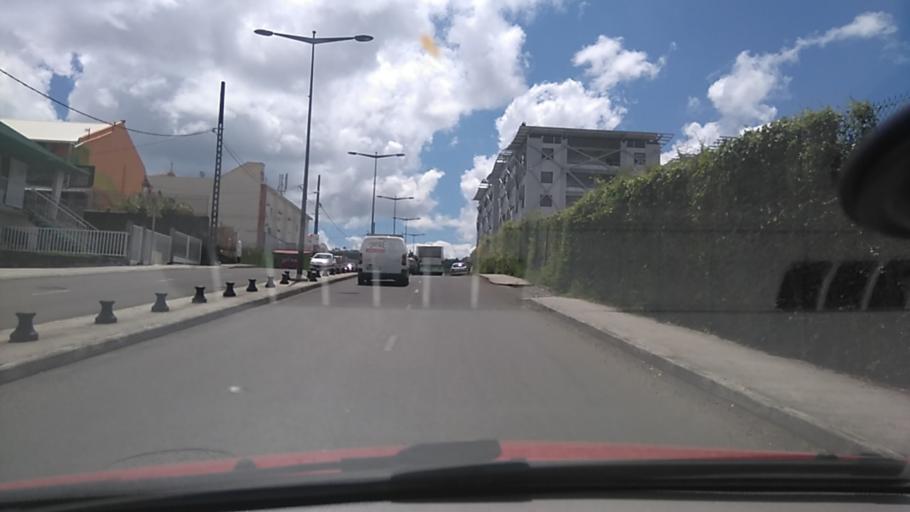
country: MQ
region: Martinique
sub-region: Martinique
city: Fort-de-France
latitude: 14.6110
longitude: -61.0512
